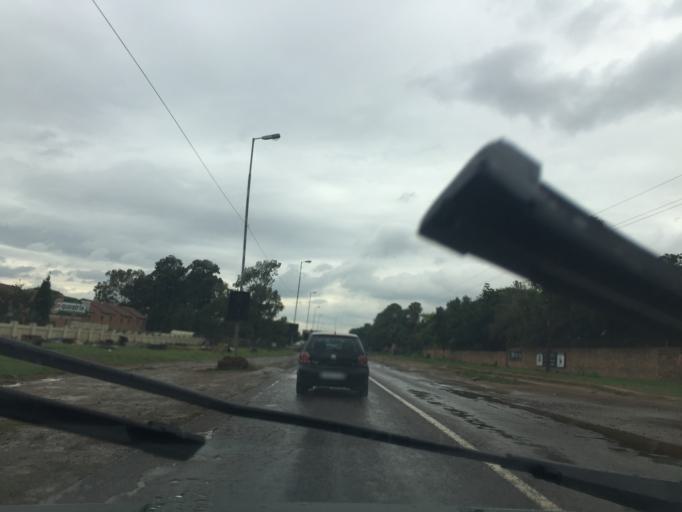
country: ZA
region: Gauteng
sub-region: City of Tshwane Metropolitan Municipality
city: Pretoria
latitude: -25.7754
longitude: 28.3390
